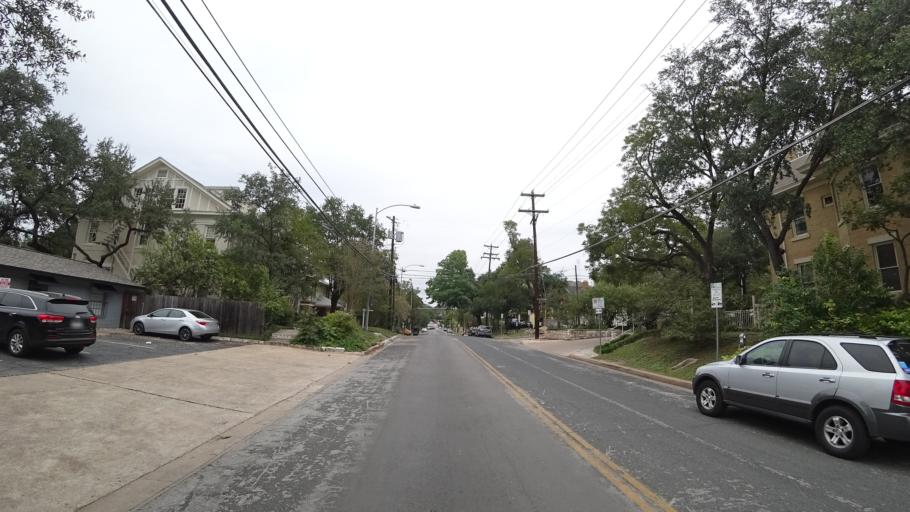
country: US
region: Texas
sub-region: Travis County
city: Austin
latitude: 30.2742
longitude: -97.7492
